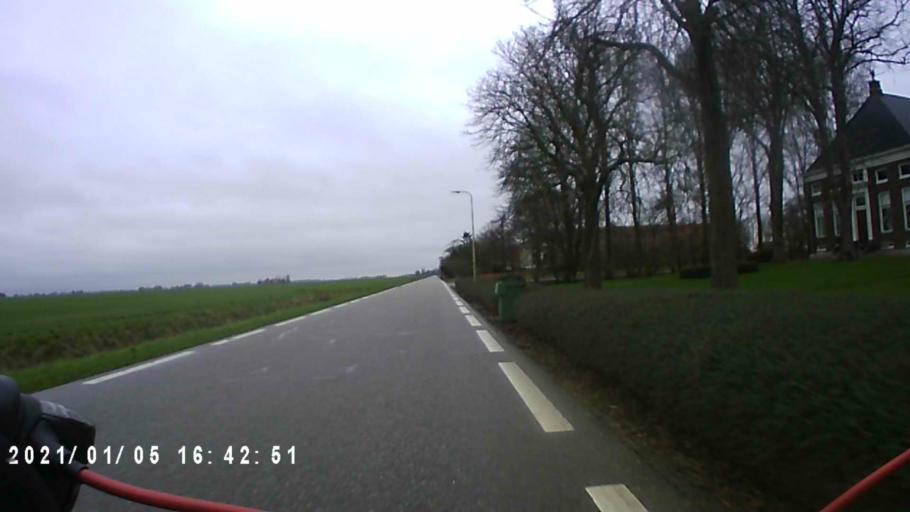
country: NL
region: Groningen
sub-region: Gemeente  Oldambt
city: Winschoten
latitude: 53.2129
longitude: 7.0512
